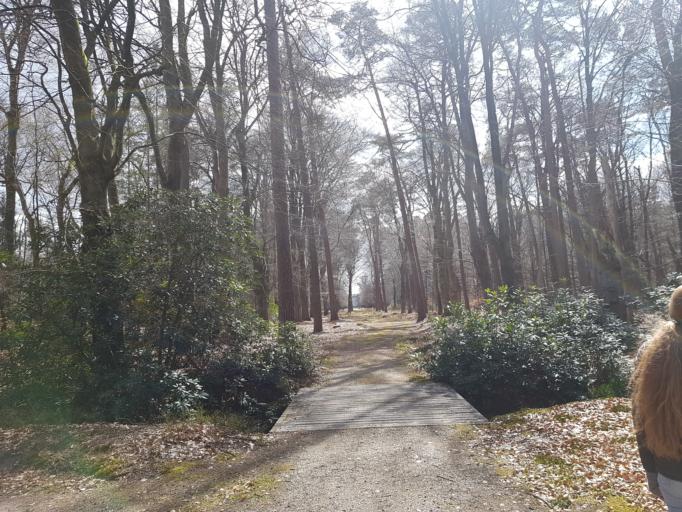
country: NL
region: Gelderland
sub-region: Gemeente Apeldoorn
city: Apeldoorn
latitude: 52.2425
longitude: 5.9458
